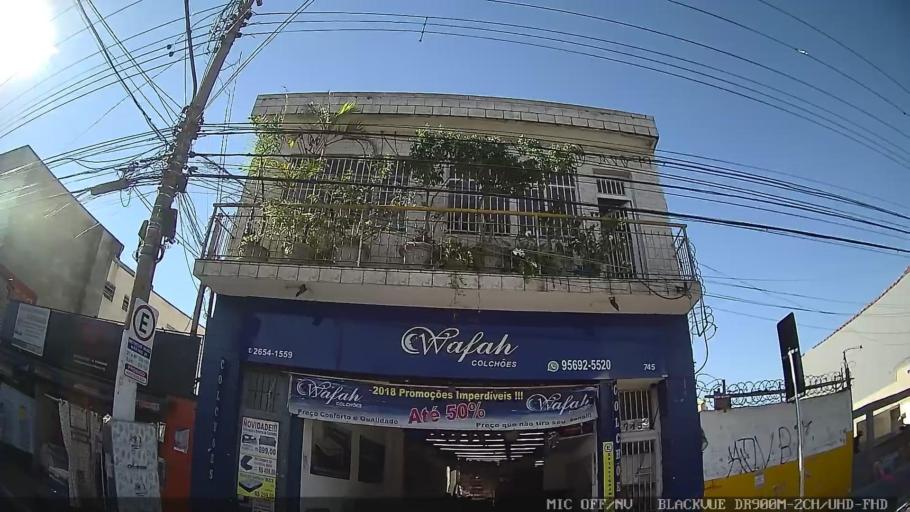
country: BR
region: Sao Paulo
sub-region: Guarulhos
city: Guarulhos
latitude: -23.5440
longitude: -46.5186
